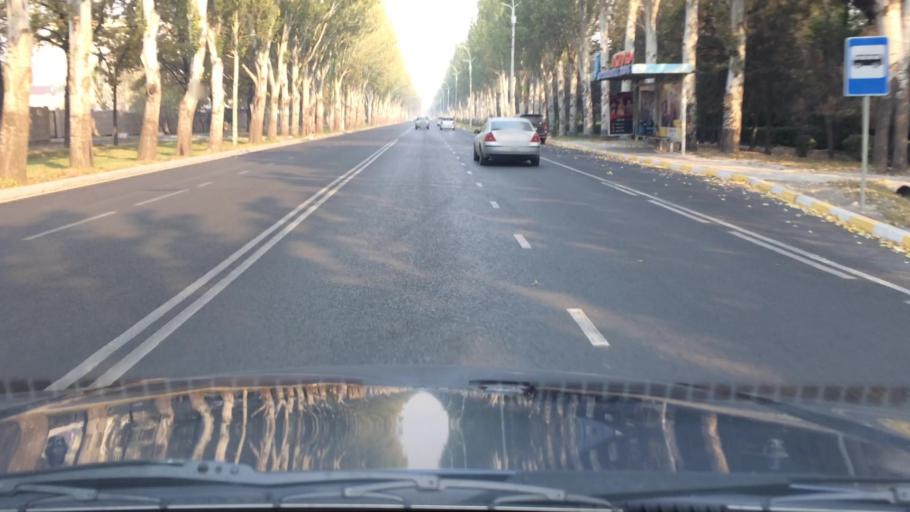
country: KG
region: Chuy
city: Bishkek
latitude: 42.8327
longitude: 74.5854
